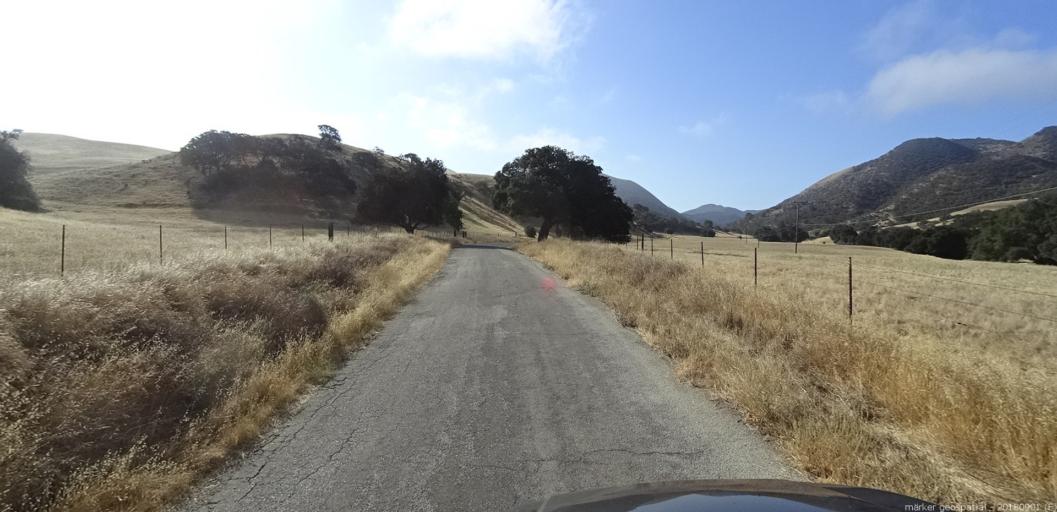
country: US
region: California
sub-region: Monterey County
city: Greenfield
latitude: 36.2484
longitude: -121.2892
